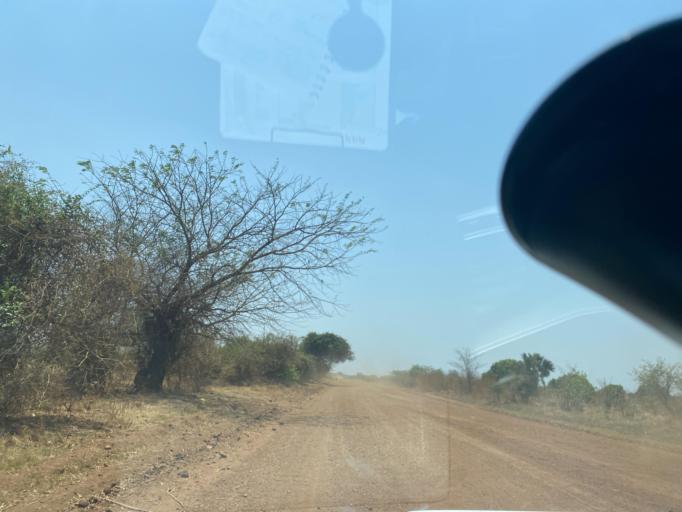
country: ZM
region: Southern
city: Nakambala
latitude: -15.4705
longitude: 27.9026
